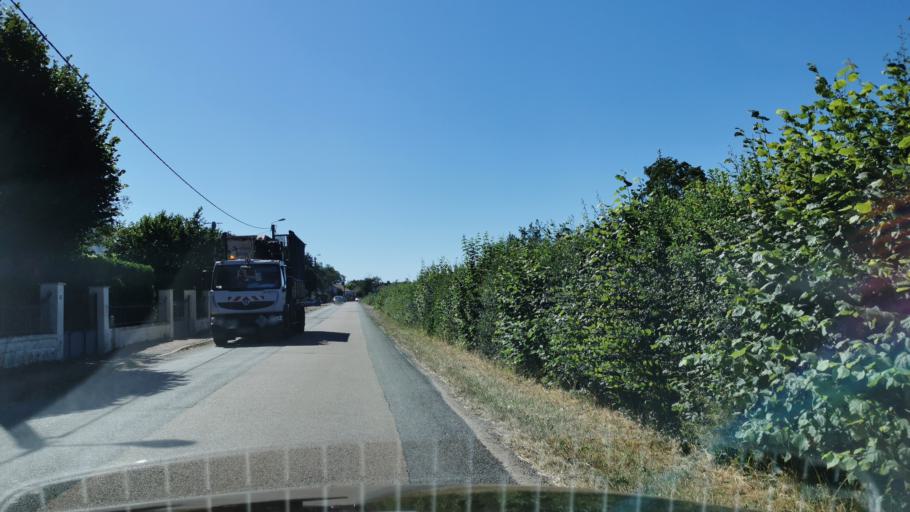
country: FR
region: Bourgogne
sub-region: Departement de Saone-et-Loire
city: Montchanin
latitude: 46.7522
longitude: 4.4917
